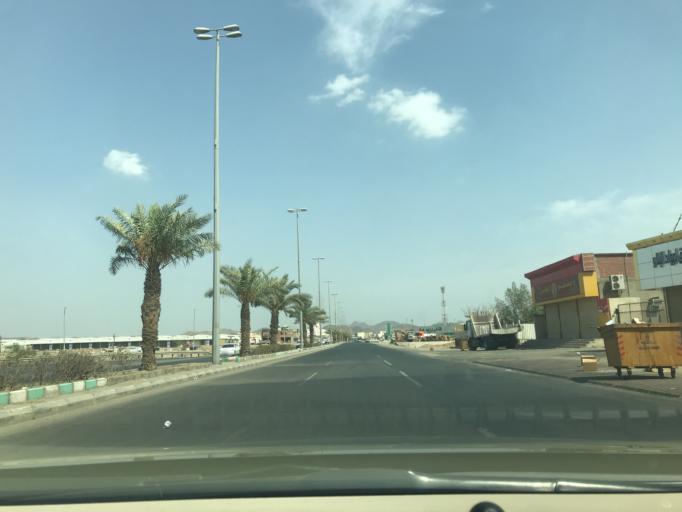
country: SA
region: Makkah
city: Al Jumum
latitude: 21.6217
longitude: 39.6841
